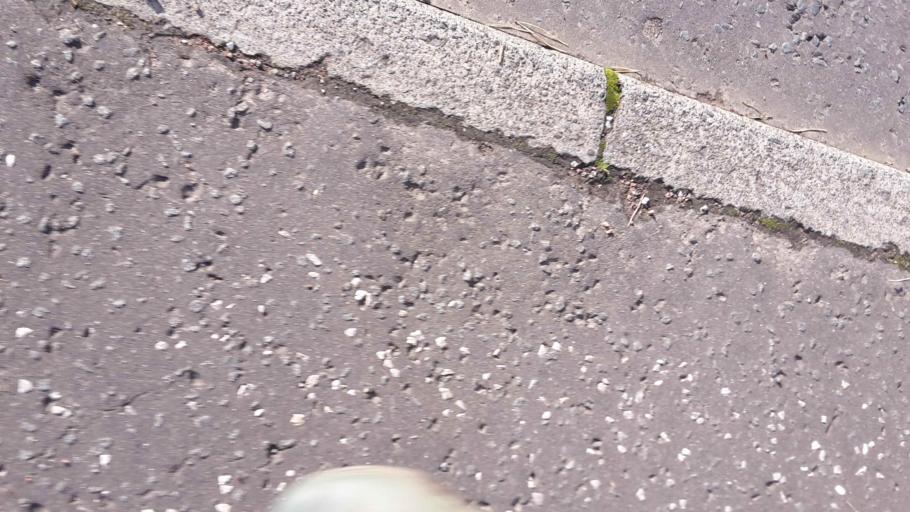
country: GB
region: Scotland
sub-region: South Lanarkshire
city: Carluke
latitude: 55.7263
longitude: -3.8368
